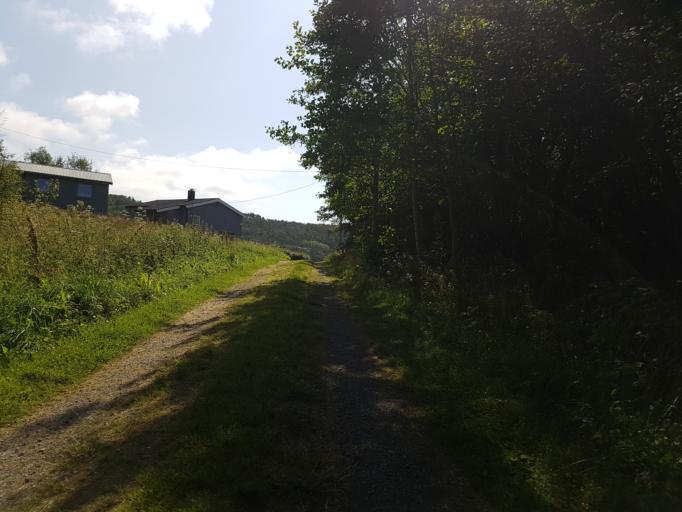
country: NO
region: Sor-Trondelag
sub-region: Agdenes
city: Lensvik
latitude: 63.6334
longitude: 9.8411
